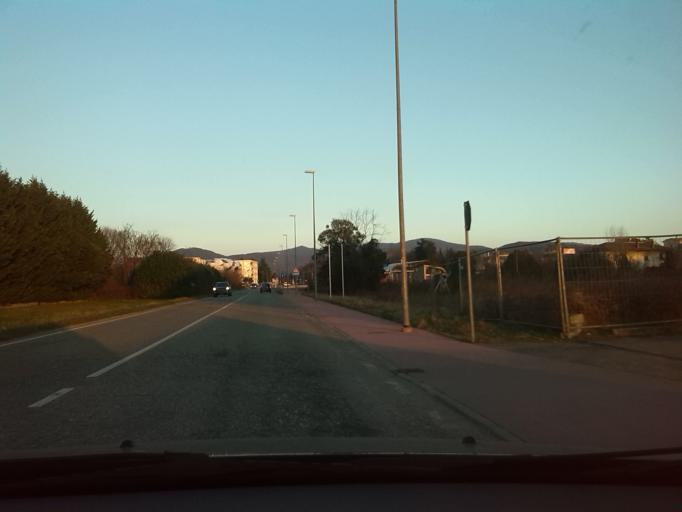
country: IT
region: Friuli Venezia Giulia
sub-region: Provincia di Udine
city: Cividale del Friuli
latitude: 46.0956
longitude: 13.4198
